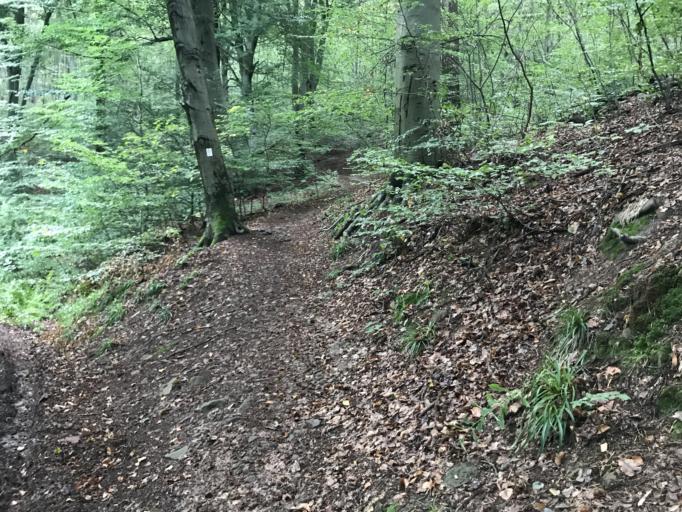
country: DE
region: Baden-Wuerttemberg
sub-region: Karlsruhe Region
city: Heidelberg
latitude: 49.4221
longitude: 8.6998
